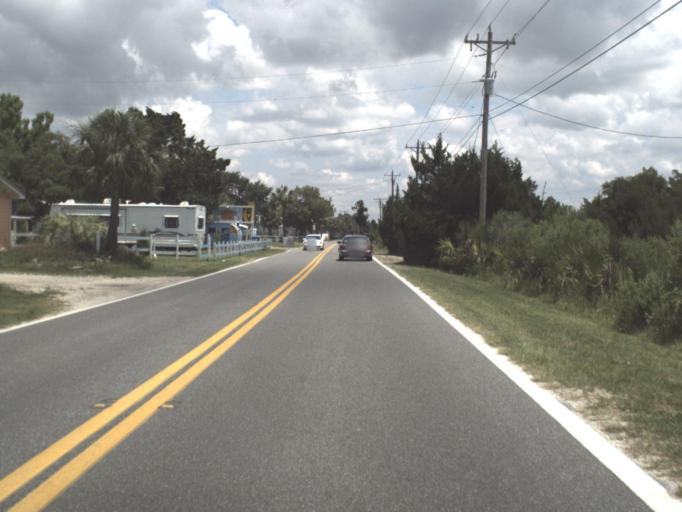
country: US
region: Florida
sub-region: Levy County
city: Chiefland
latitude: 29.1536
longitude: -83.0305
